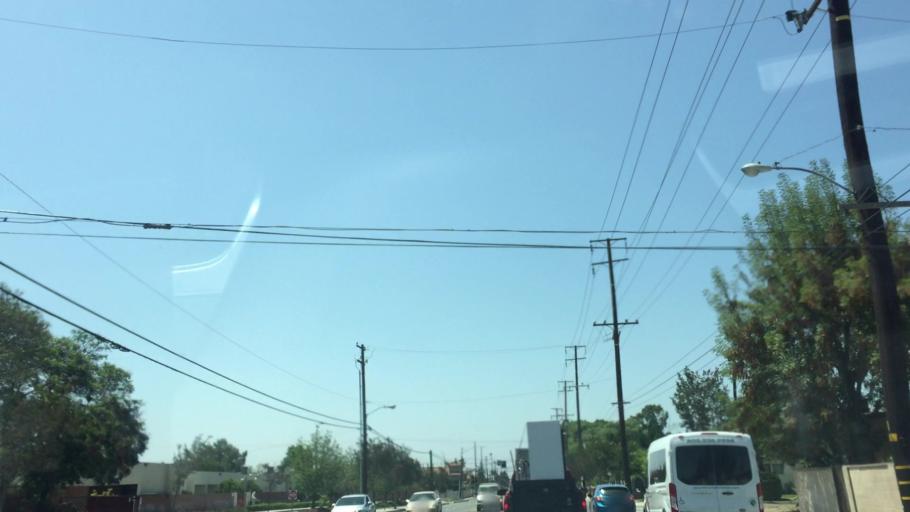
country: US
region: California
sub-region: Orange County
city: Garden Grove
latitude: 33.7544
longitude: -117.9290
